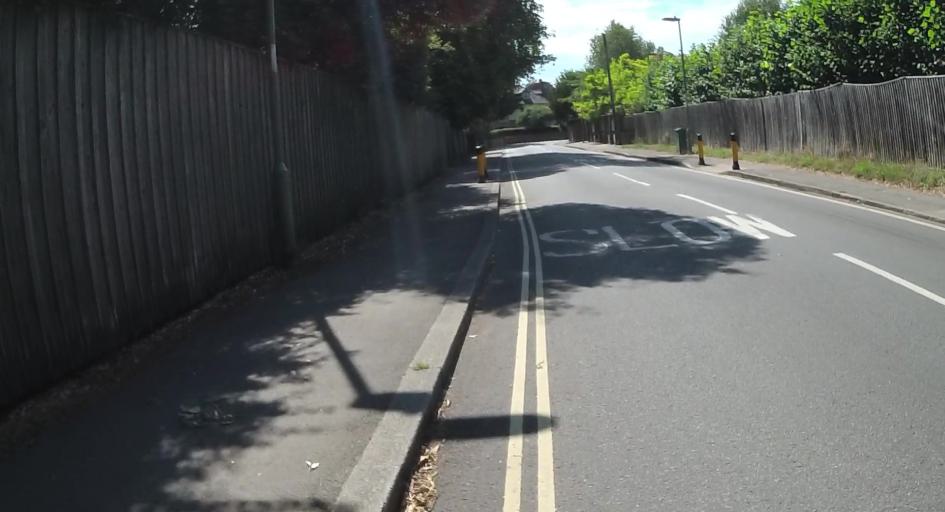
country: GB
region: England
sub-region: Hampshire
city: Winchester
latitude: 51.0528
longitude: -1.3197
